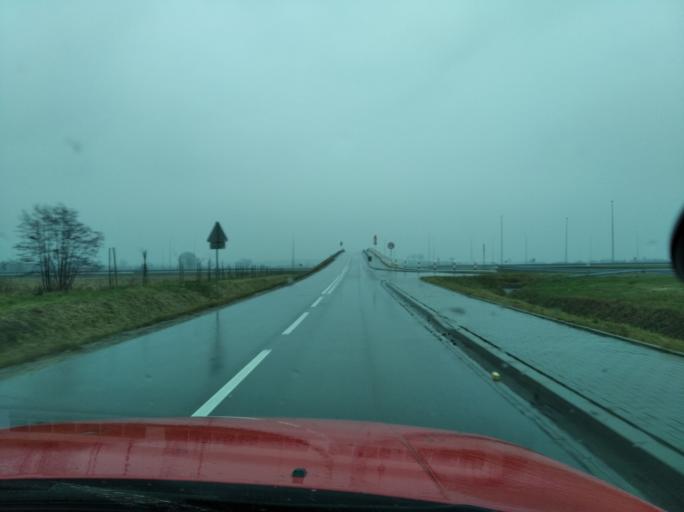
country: PL
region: Subcarpathian Voivodeship
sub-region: Powiat lancucki
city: Czarna
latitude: 50.0921
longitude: 22.1704
